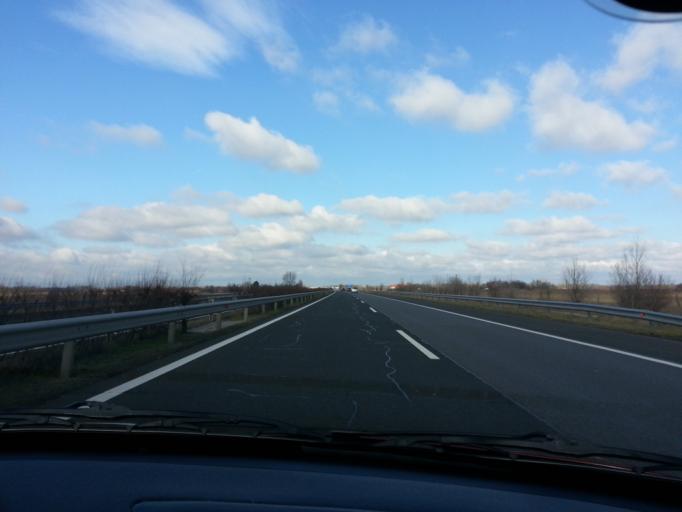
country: HU
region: Csongrad
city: Balastya
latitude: 46.3916
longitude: 19.9847
